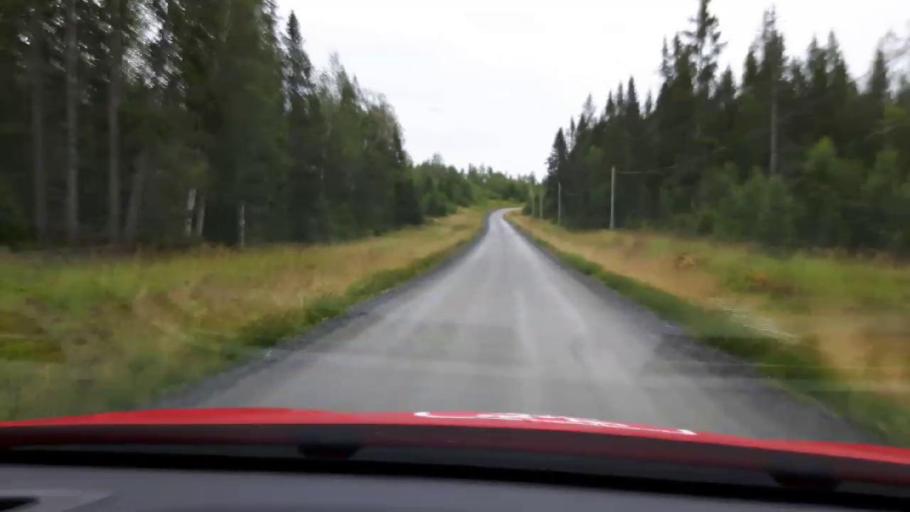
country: SE
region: Jaemtland
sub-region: Are Kommun
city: Are
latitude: 63.4956
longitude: 12.7639
